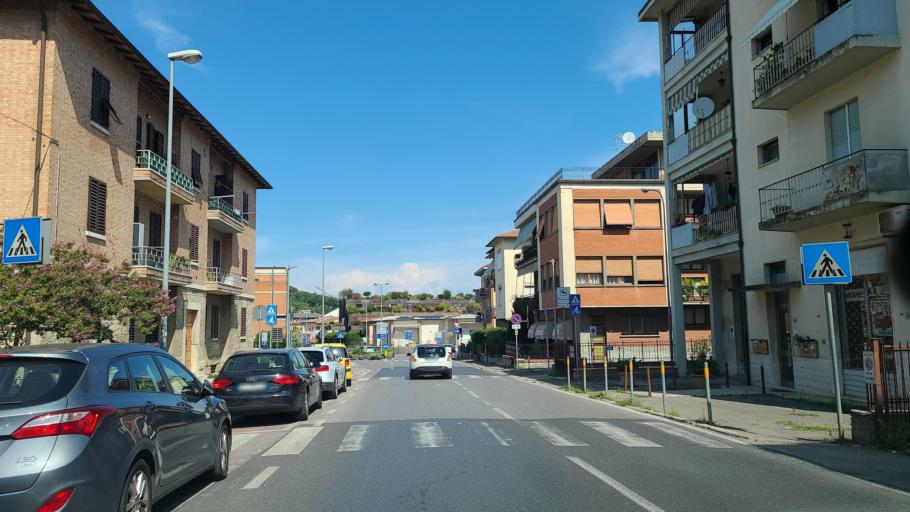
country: IT
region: Tuscany
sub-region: Provincia di Siena
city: Colle di Val d'Elsa
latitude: 43.4209
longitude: 11.1293
